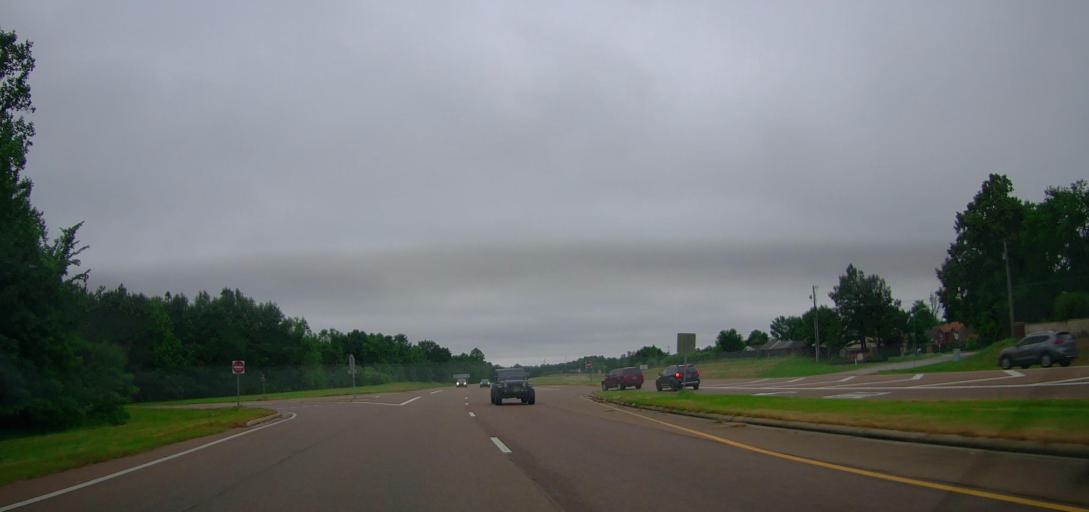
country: US
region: Mississippi
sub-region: De Soto County
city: Olive Branch
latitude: 34.9636
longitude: -89.7996
